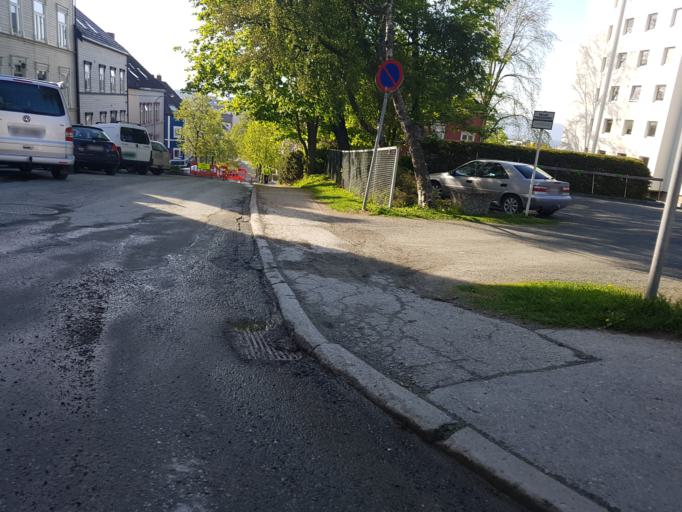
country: NO
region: Sor-Trondelag
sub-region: Trondheim
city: Trondheim
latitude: 63.4333
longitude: 10.4200
